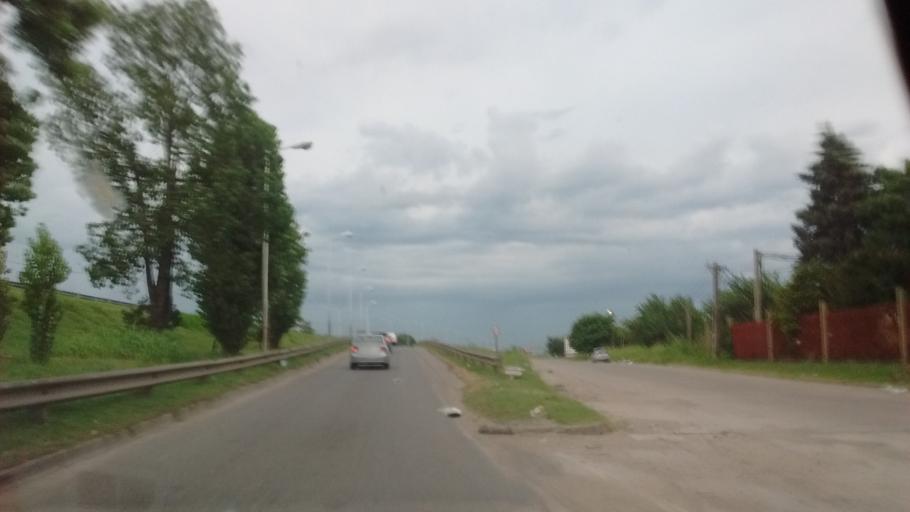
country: AR
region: Santa Fe
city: Perez
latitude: -32.9693
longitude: -60.7171
